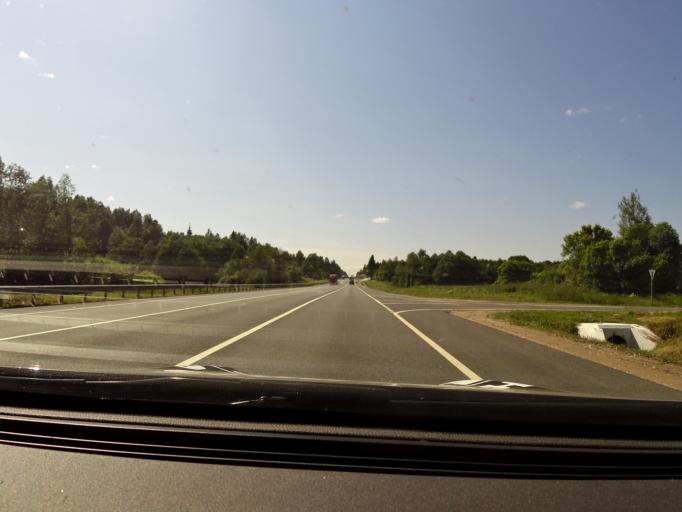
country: RU
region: Novgorod
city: Kresttsy
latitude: 58.3672
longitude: 32.1437
